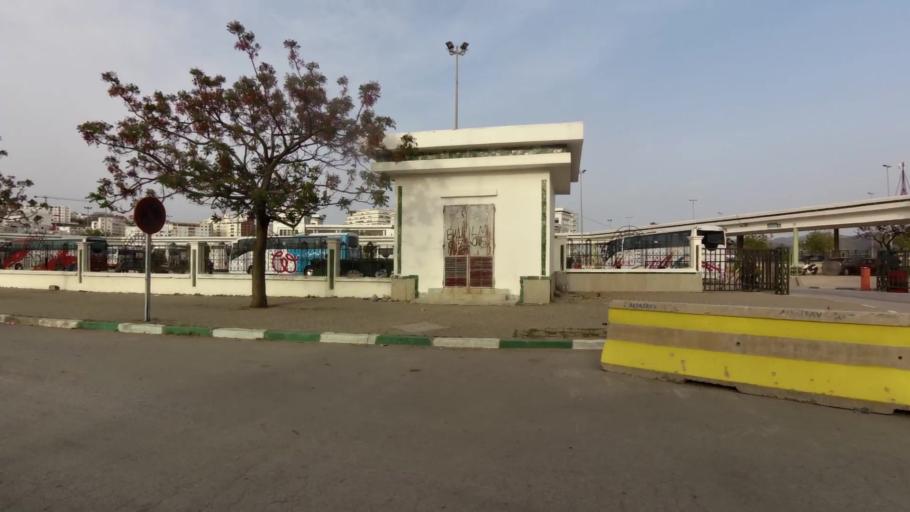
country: MA
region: Tanger-Tetouan
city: Tetouan
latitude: 35.5603
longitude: -5.3727
